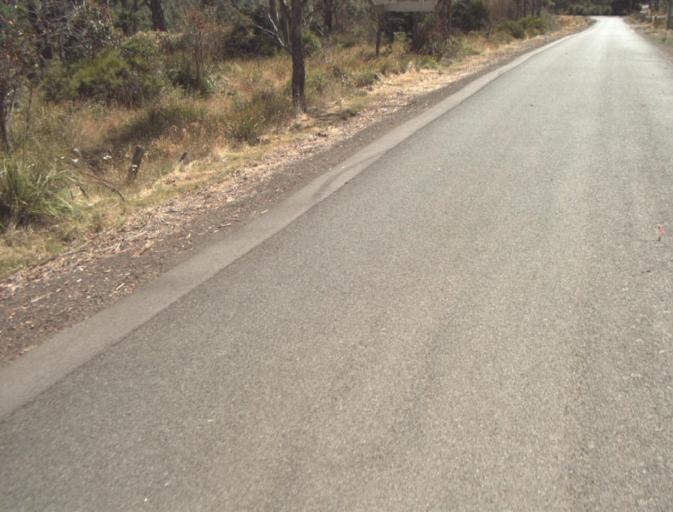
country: AU
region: Tasmania
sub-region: Launceston
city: Newstead
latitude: -41.3849
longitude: 147.2970
